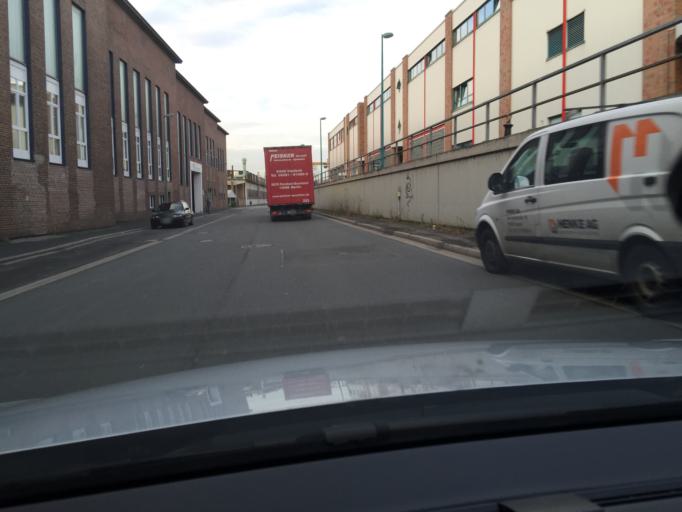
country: DE
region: North Rhine-Westphalia
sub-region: Regierungsbezirk Arnsberg
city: Hagen
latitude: 51.3715
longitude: 7.4549
